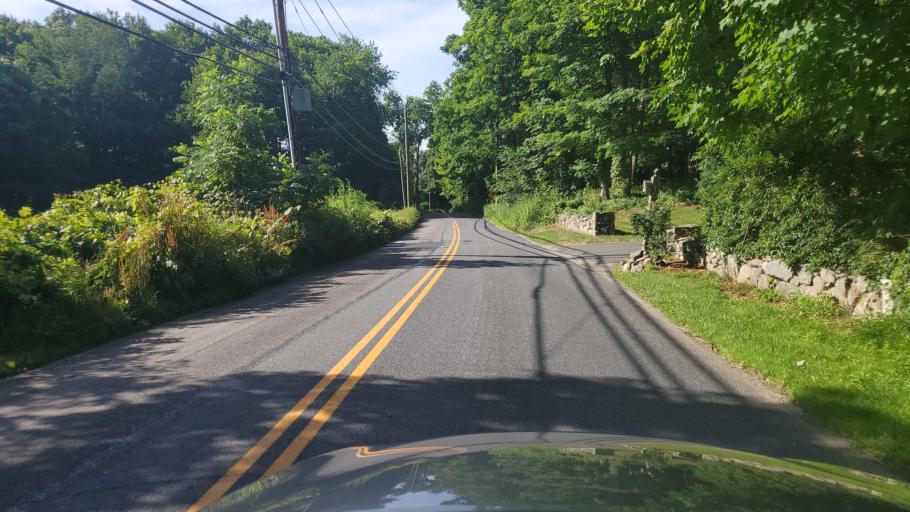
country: US
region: Connecticut
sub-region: Fairfield County
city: Newtown
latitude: 41.3803
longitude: -73.3131
